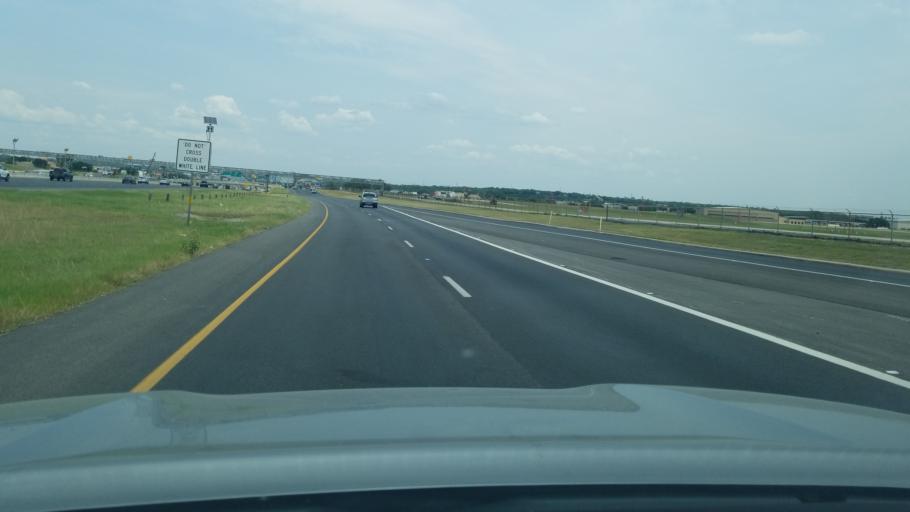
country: US
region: Texas
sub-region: Bexar County
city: Castle Hills
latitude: 29.5435
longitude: -98.4902
